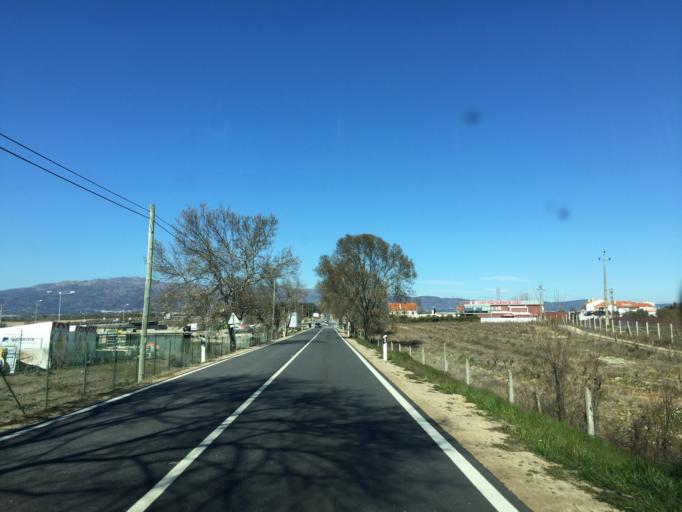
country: PT
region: Guarda
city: Alcains
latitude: 39.9844
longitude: -7.4580
